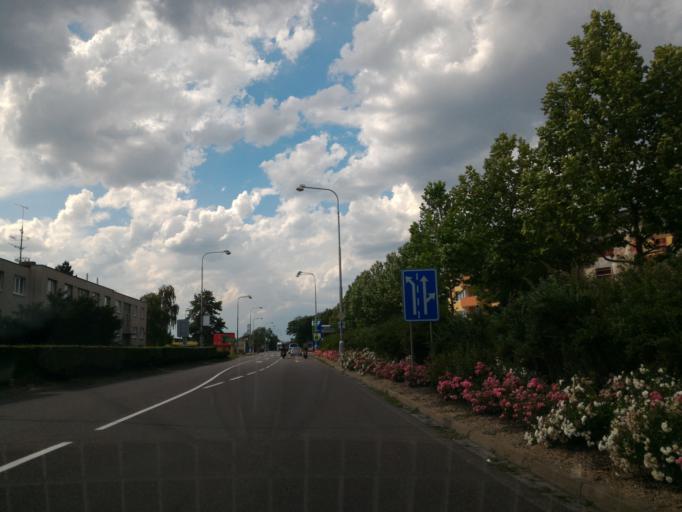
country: CZ
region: South Moravian
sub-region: Okres Znojmo
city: Znojmo
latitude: 48.8673
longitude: 16.0347
